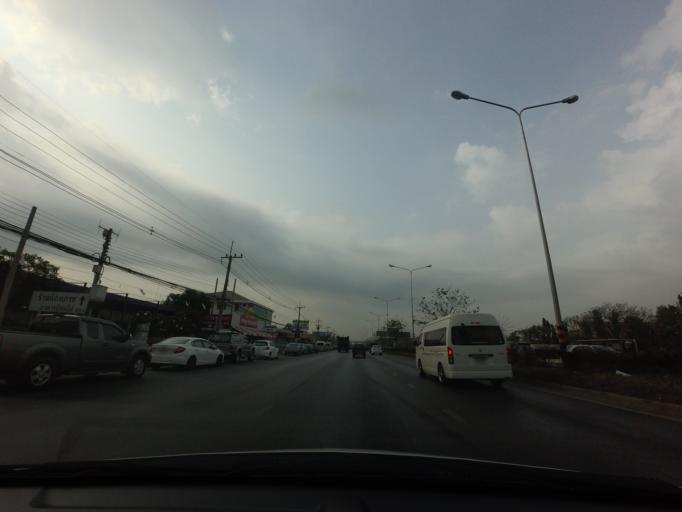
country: TH
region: Bangkok
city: Thawi Watthana
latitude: 13.7726
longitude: 100.3283
